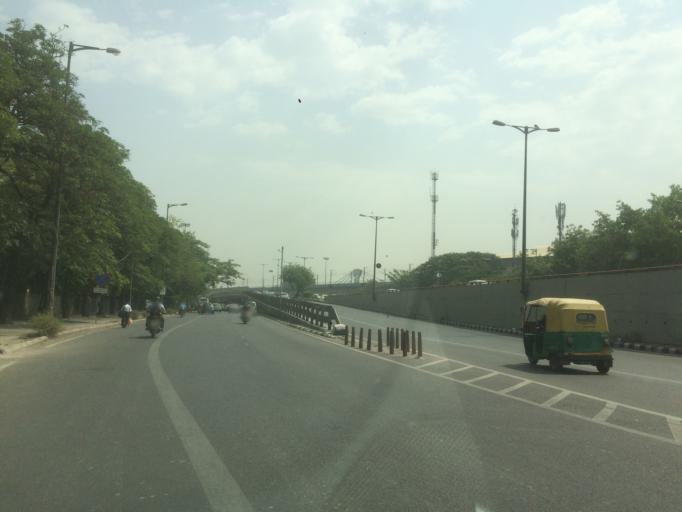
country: IN
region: NCT
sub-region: New Delhi
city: New Delhi
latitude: 28.5634
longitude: 77.2328
